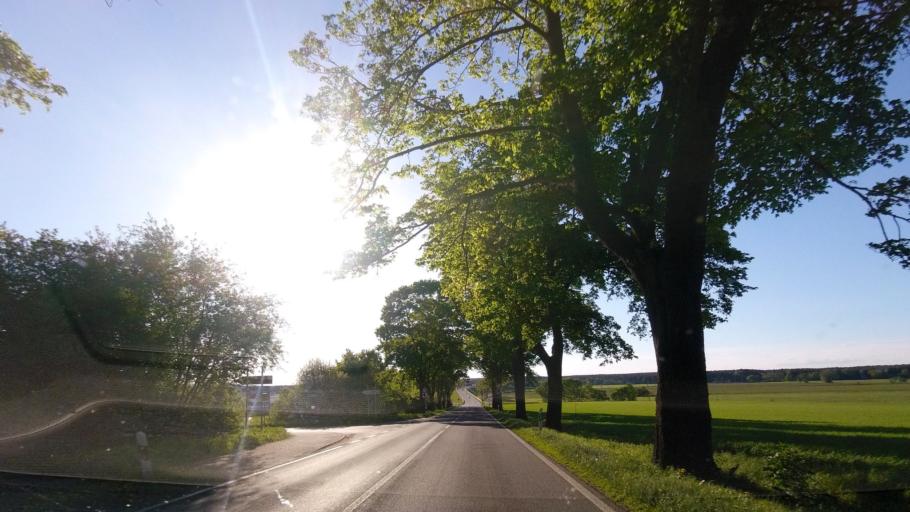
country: DE
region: Brandenburg
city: Golssen
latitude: 51.9803
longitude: 13.5777
